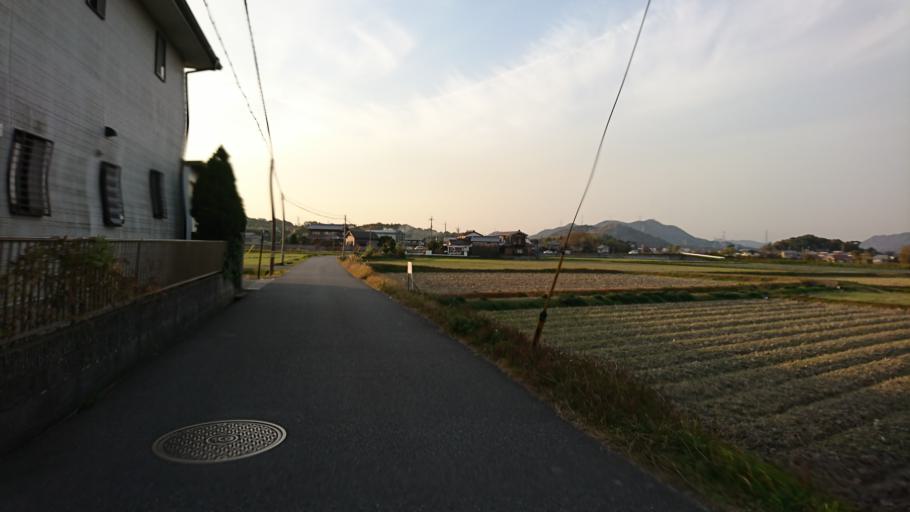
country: JP
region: Hyogo
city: Kakogawacho-honmachi
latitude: 34.7791
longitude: 134.8751
